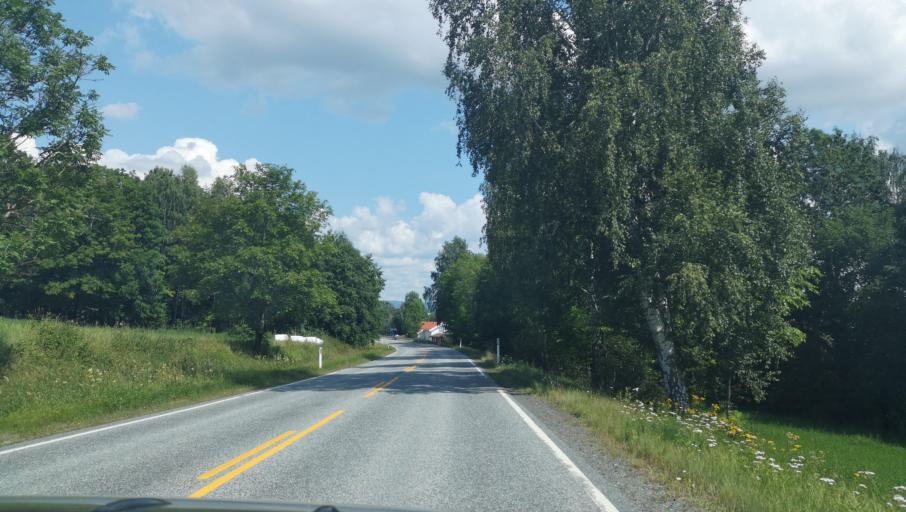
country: NO
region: Buskerud
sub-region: Ovre Eiker
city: Hokksund
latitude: 59.7085
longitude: 9.8151
